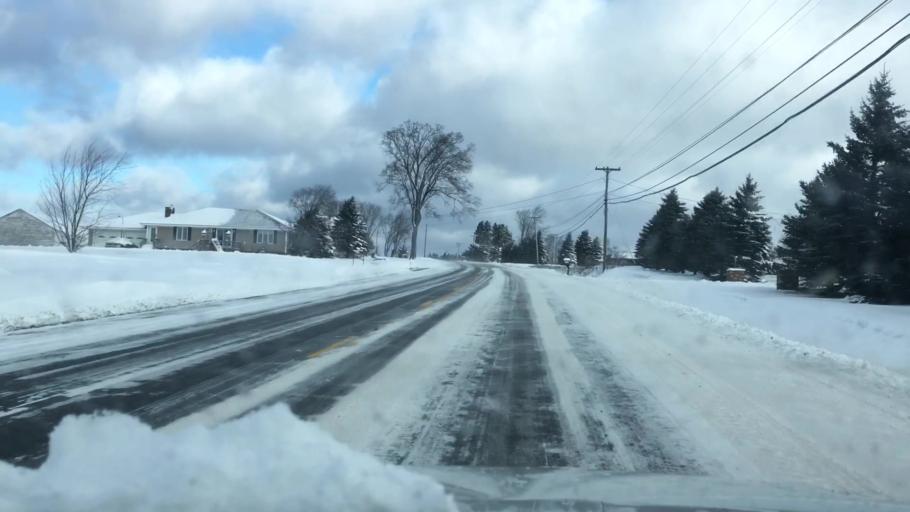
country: US
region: Maine
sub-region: Aroostook County
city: Caribou
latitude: 46.9004
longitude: -68.0153
